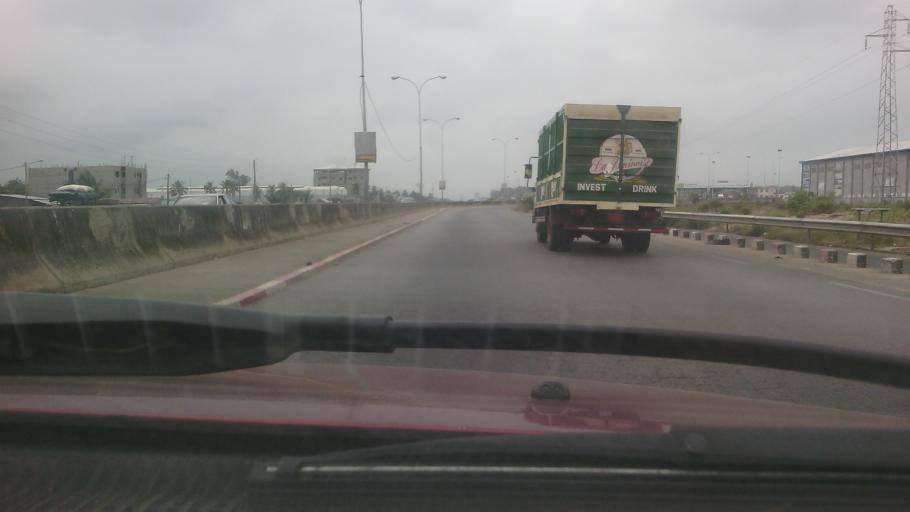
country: BJ
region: Littoral
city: Cotonou
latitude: 6.3715
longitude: 2.5310
